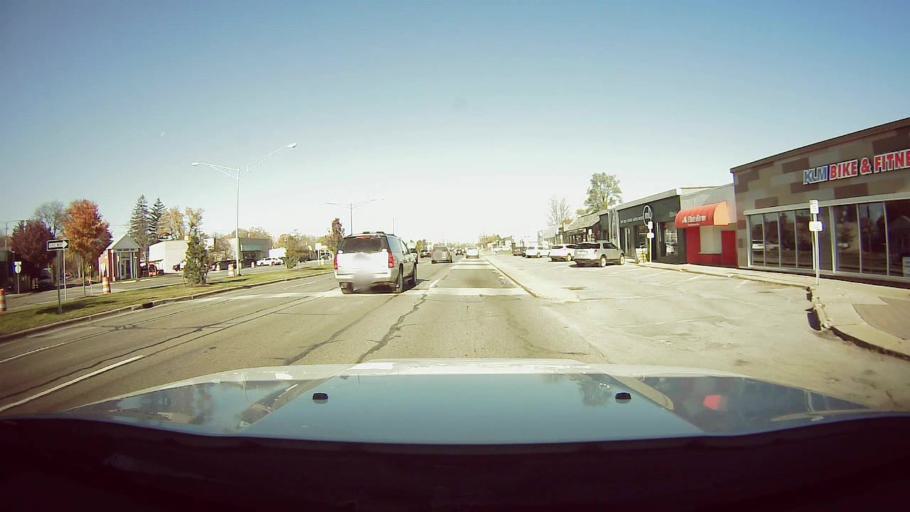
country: US
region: Michigan
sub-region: Oakland County
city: Birmingham
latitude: 42.5359
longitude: -83.2033
